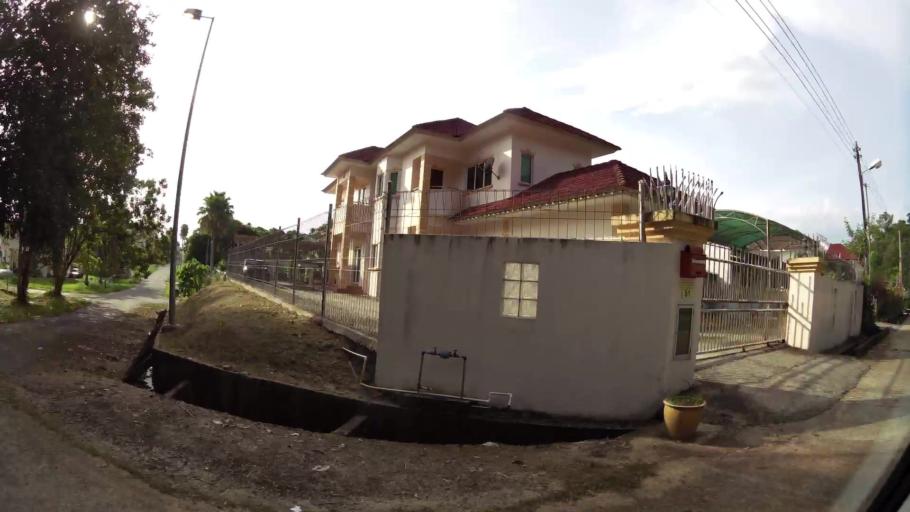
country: BN
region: Brunei and Muara
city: Bandar Seri Begawan
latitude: 4.9667
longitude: 114.9834
